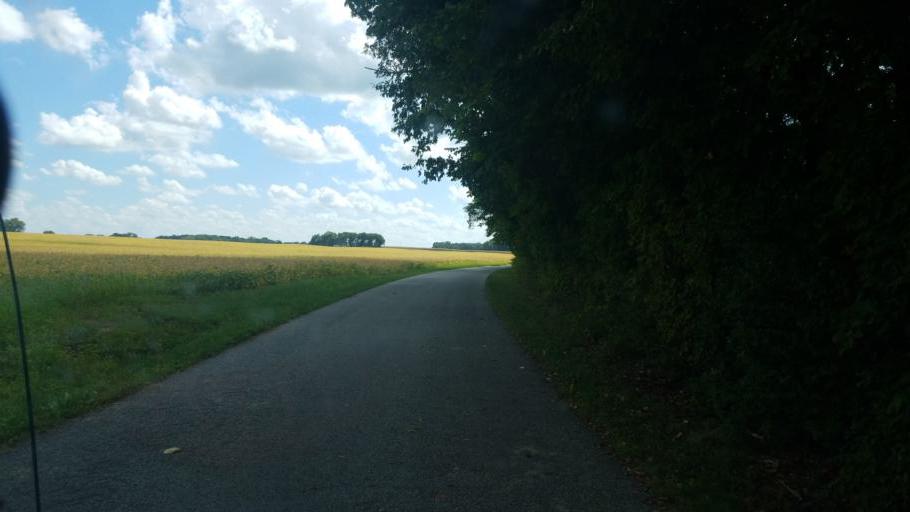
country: US
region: Ohio
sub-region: Marion County
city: Prospect
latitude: 40.4262
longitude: -83.1915
